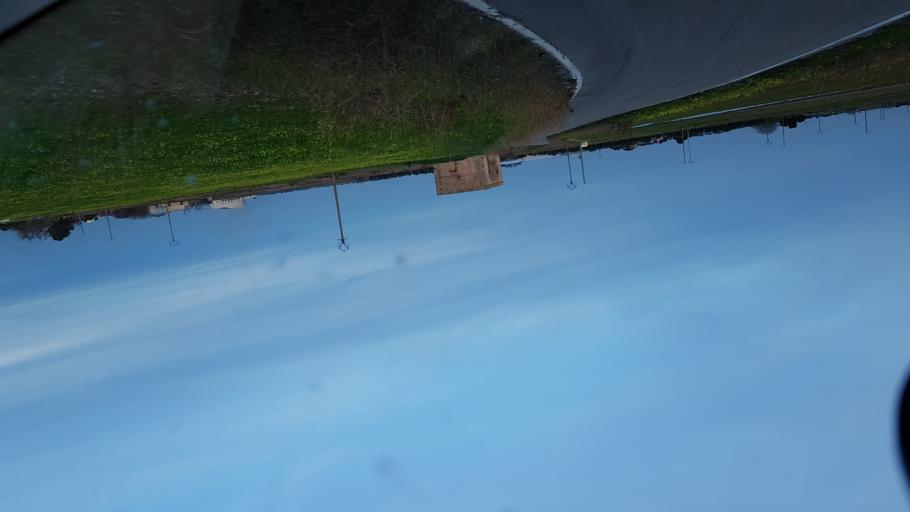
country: IT
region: Apulia
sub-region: Provincia di Brindisi
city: Brindisi
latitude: 40.6602
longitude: 17.9109
